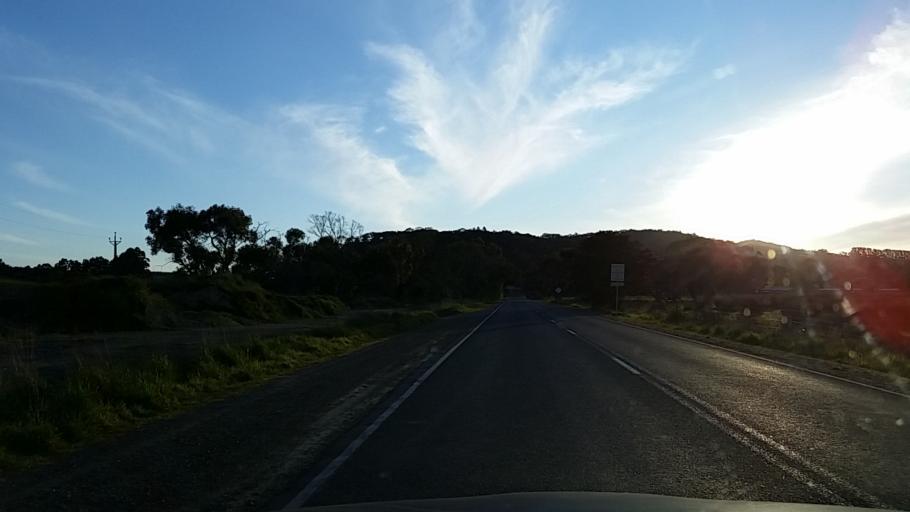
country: AU
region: South Australia
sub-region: Alexandrina
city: Mount Compass
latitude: -35.3394
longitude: 138.6572
